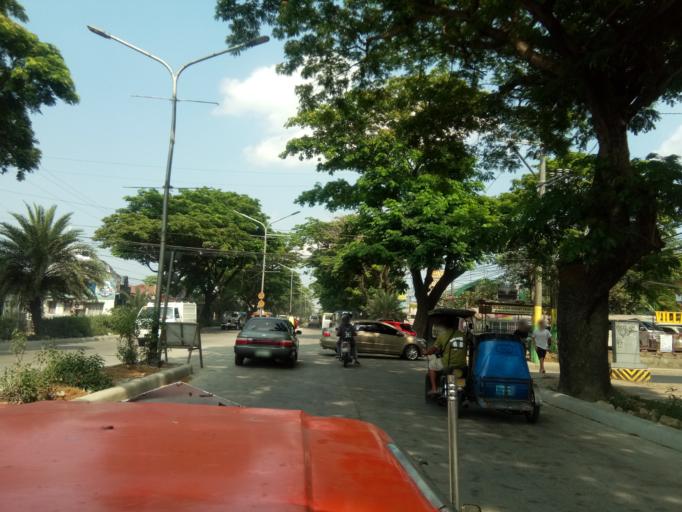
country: PH
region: Calabarzon
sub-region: Province of Cavite
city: Dasmarinas
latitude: 14.3268
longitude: 120.9481
